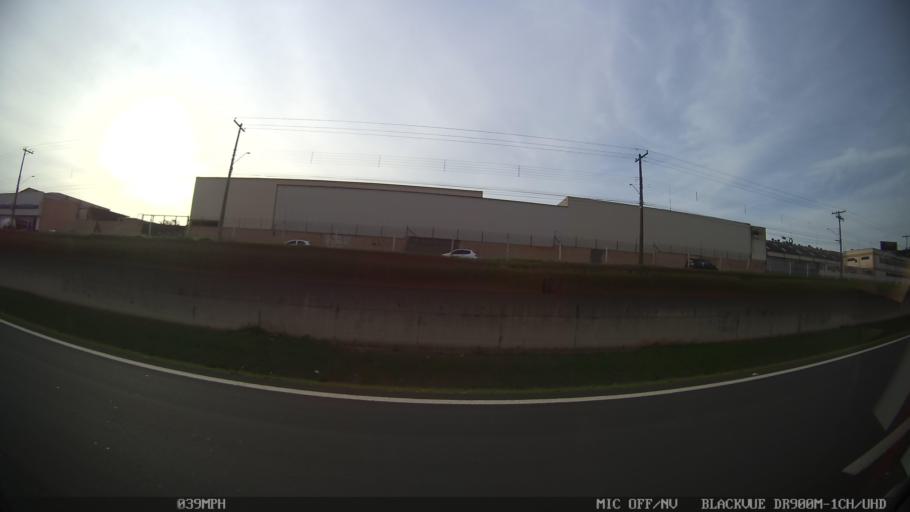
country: BR
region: Sao Paulo
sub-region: Limeira
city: Limeira
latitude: -22.5639
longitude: -47.4268
